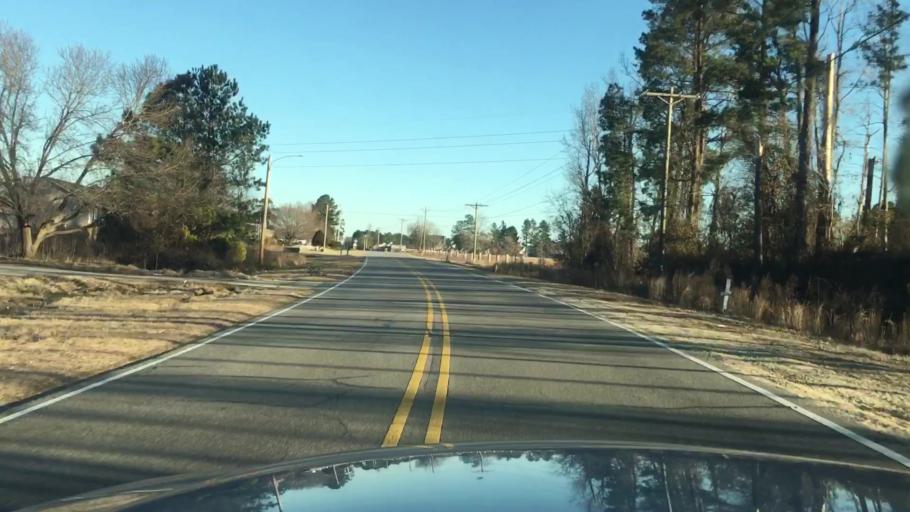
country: US
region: North Carolina
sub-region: Cumberland County
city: Hope Mills
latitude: 34.9653
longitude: -79.0079
